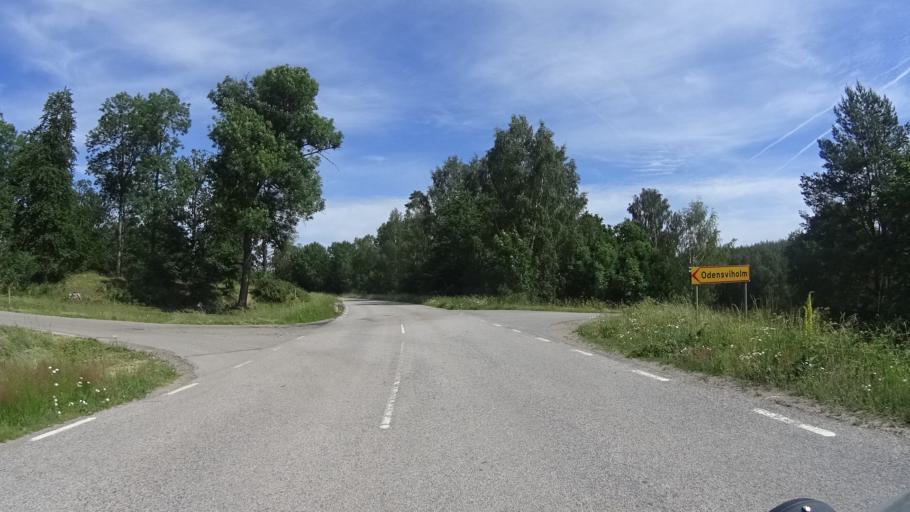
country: SE
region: Kalmar
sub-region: Vasterviks Kommun
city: Overum
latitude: 57.9058
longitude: 16.1758
